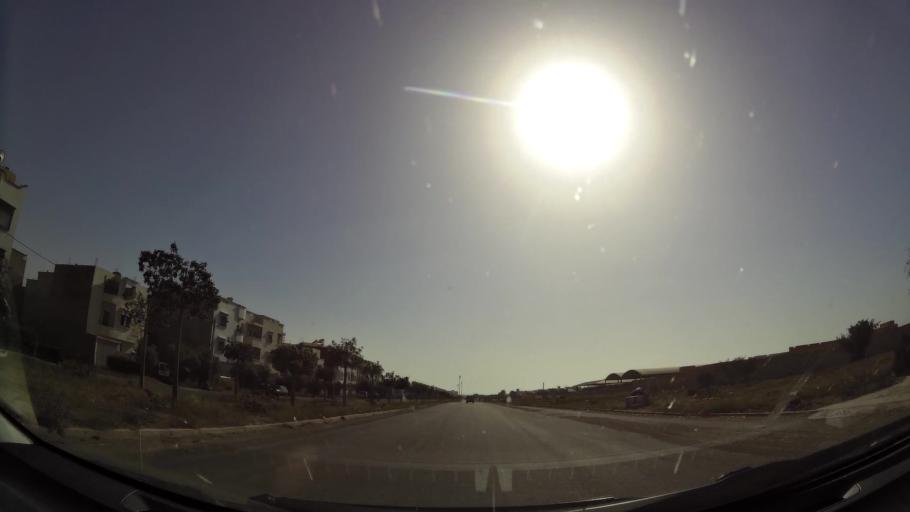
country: MA
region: Souss-Massa-Draa
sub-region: Inezgane-Ait Mellou
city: Inezgane
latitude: 30.3833
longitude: -9.5107
